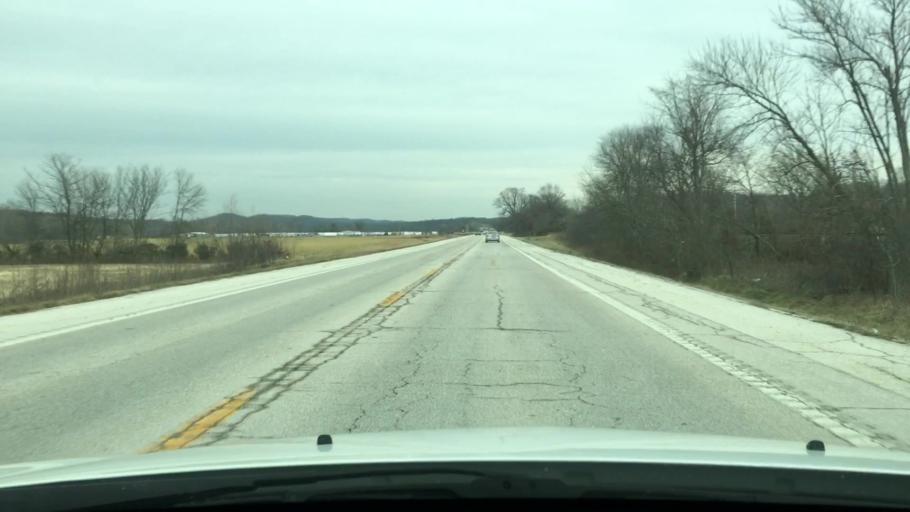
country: US
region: Missouri
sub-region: Pike County
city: Bowling Green
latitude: 39.3800
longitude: -91.1403
